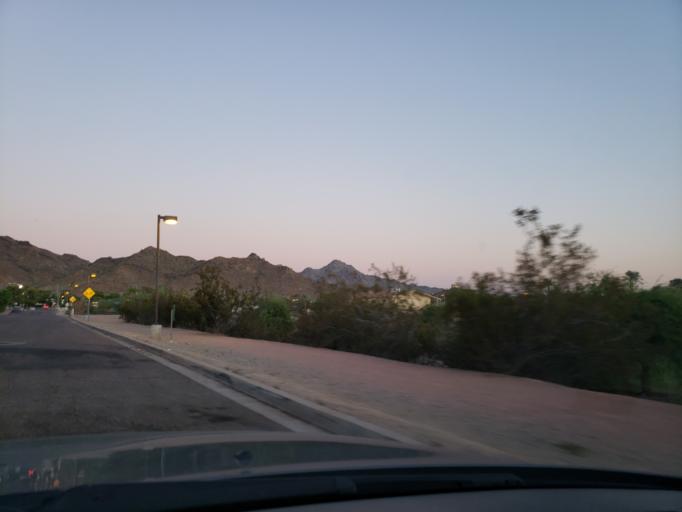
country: US
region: Arizona
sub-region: Maricopa County
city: Phoenix
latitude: 33.5659
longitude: -112.0616
